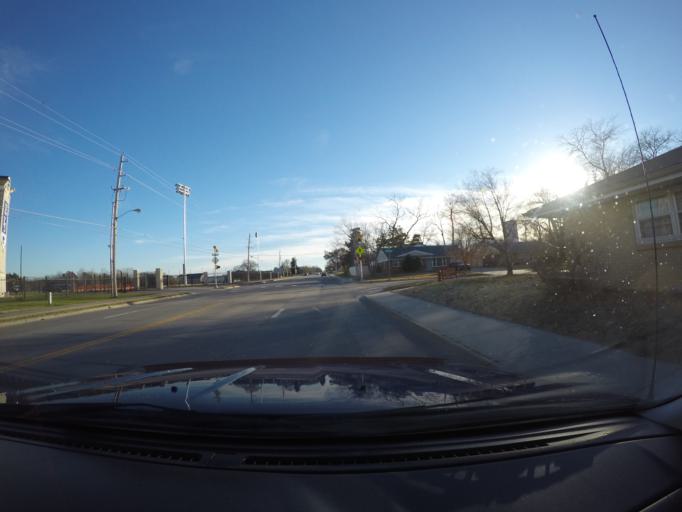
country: US
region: Kansas
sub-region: Riley County
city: Manhattan
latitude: 39.1989
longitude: -96.5983
